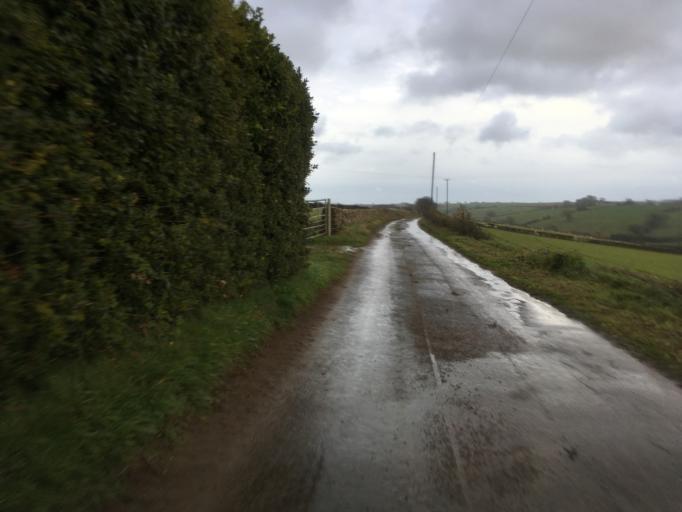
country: GB
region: England
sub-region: South Gloucestershire
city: Cold Ashton
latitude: 51.4679
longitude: -2.3483
